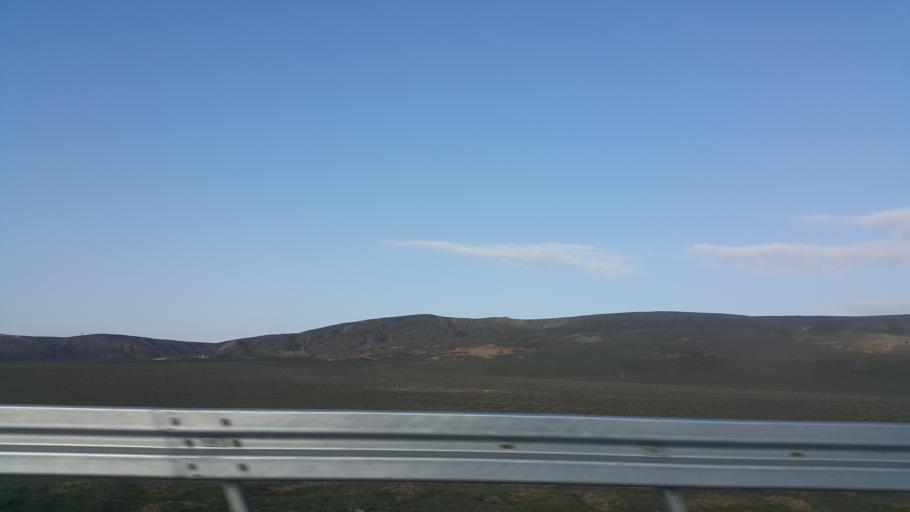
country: TR
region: Konya
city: Kulu
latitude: 39.1383
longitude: 33.3401
